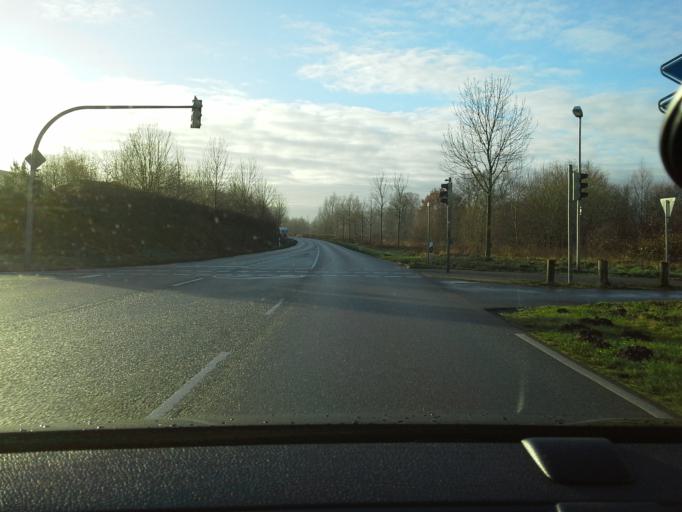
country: DE
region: Schleswig-Holstein
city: Pinneberg
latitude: 53.6515
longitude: 9.7697
